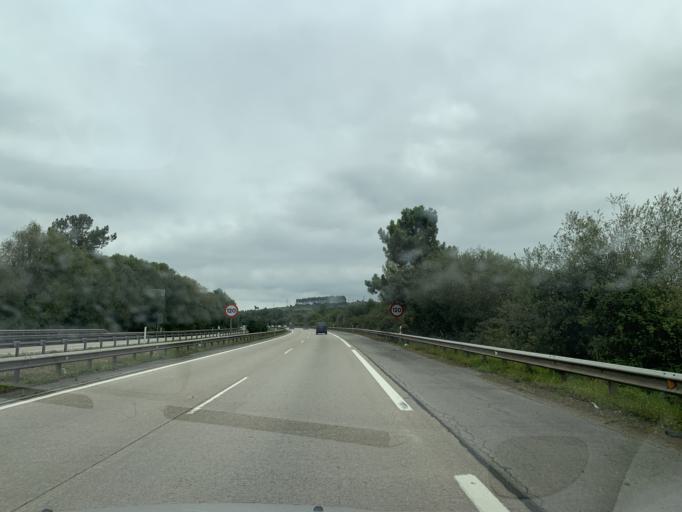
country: ES
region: Asturias
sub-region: Province of Asturias
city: Corvera de Asturias
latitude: 43.5205
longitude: -5.8226
